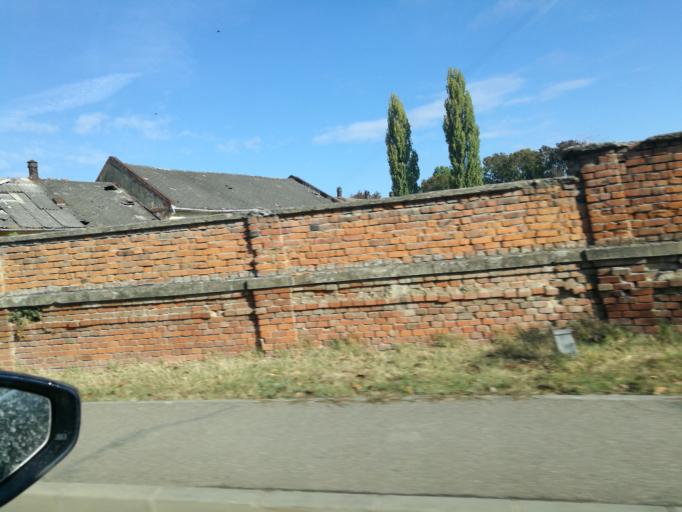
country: RO
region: Bihor
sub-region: Comuna Biharea
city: Oradea
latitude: 47.0421
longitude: 21.9223
